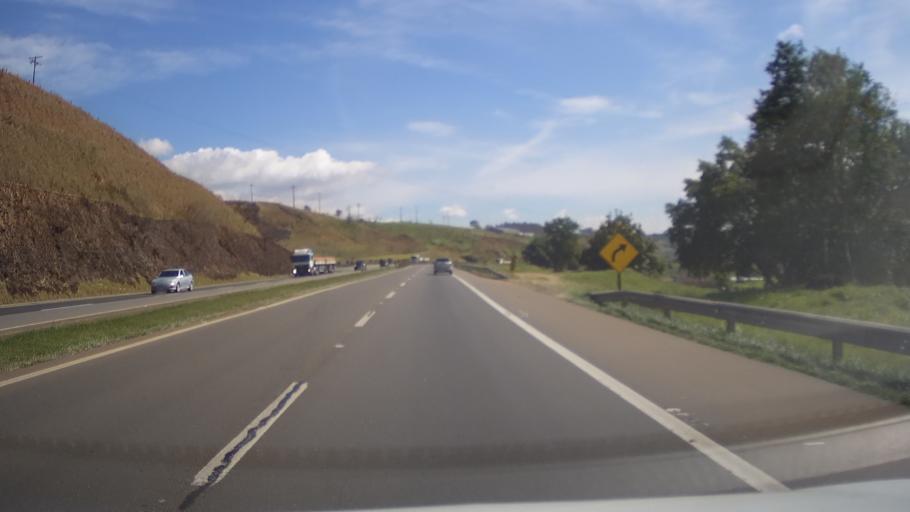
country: BR
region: Minas Gerais
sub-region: Cambui
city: Cambui
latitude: -22.5480
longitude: -46.0399
